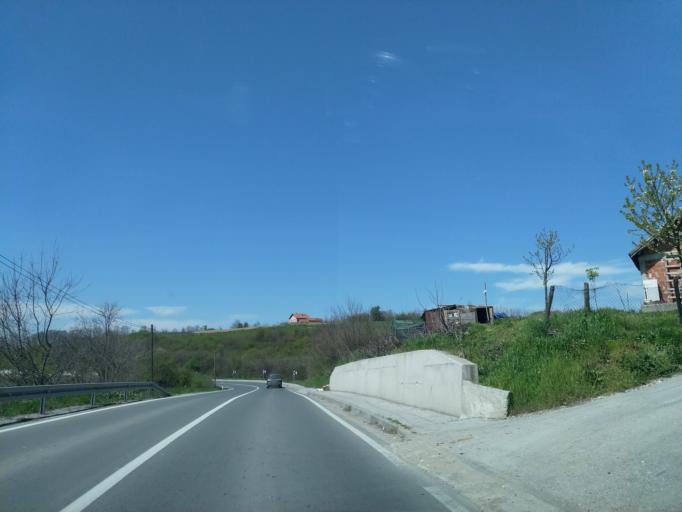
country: RS
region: Central Serbia
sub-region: Sumadijski Okrug
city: Arangelovac
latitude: 44.3349
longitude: 20.4953
